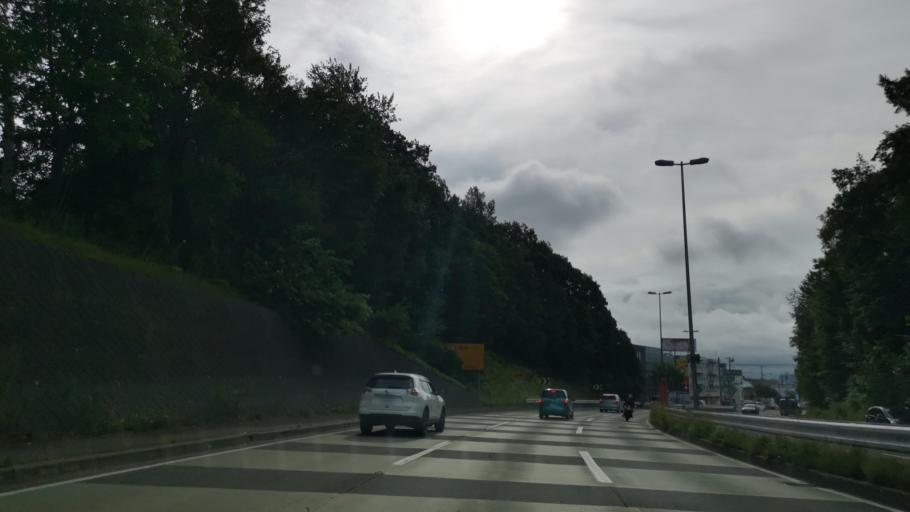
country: JP
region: Hokkaido
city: Sapporo
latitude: 43.0050
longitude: 141.4251
